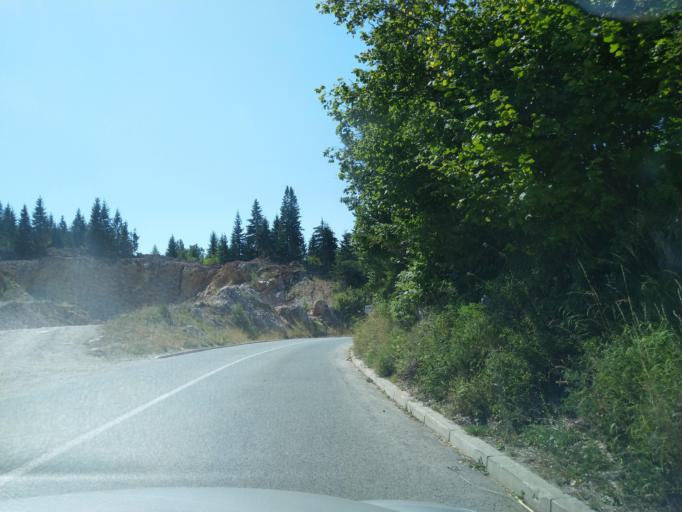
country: RS
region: Central Serbia
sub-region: Zlatiborski Okrug
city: Nova Varos
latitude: 43.4054
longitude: 19.8439
